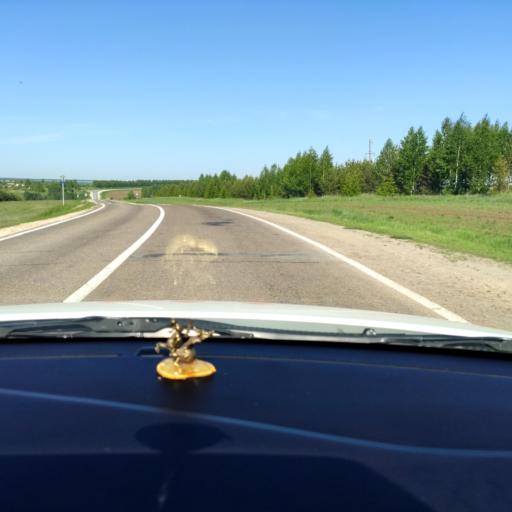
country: RU
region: Tatarstan
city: Vysokaya Gora
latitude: 56.0171
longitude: 49.2787
